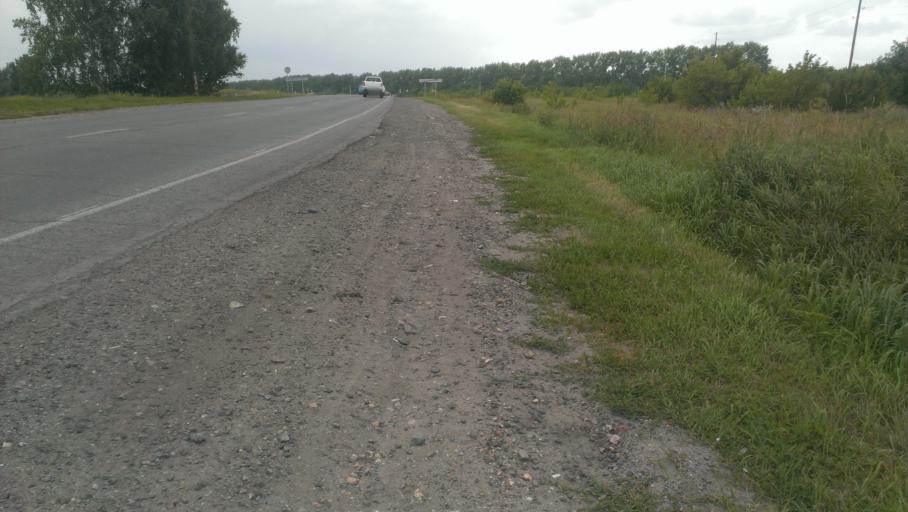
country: RU
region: Altai Krai
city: Gon'ba
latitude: 53.3900
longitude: 83.6011
